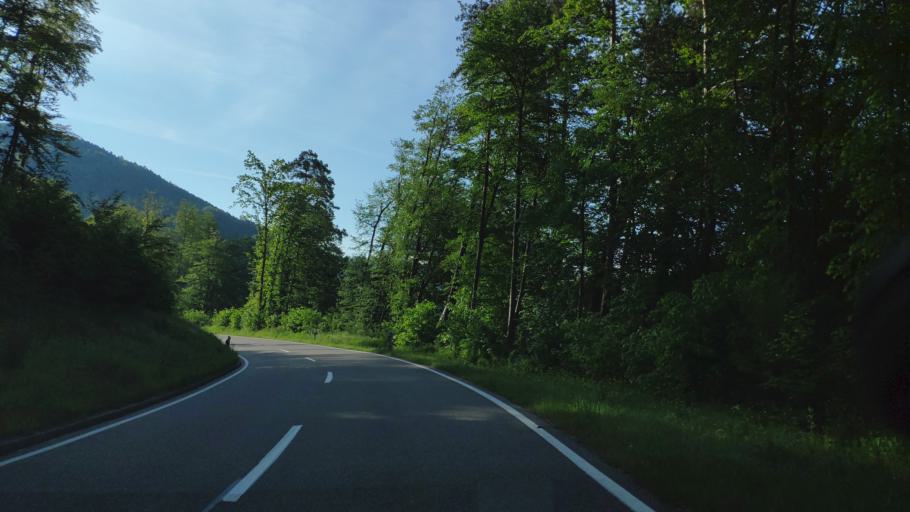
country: DE
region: Rheinland-Pfalz
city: Fischbach
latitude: 49.0842
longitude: 7.7297
